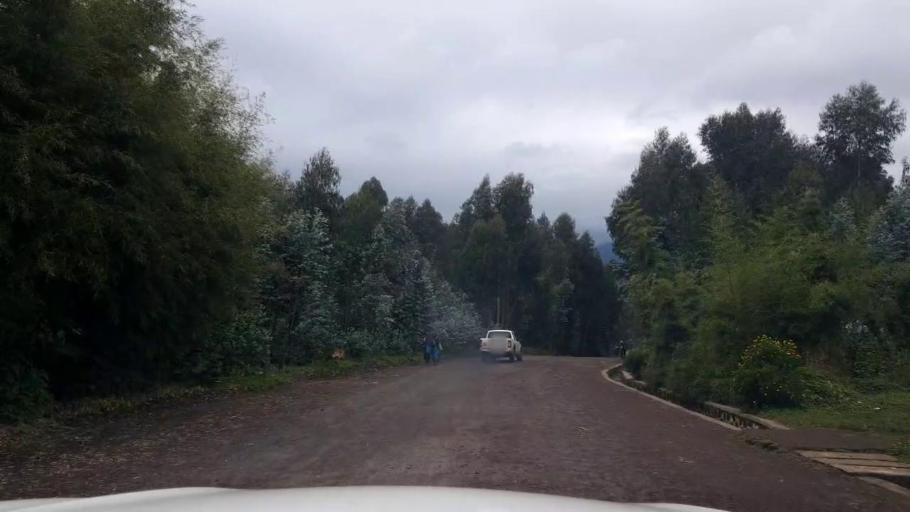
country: RW
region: Northern Province
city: Musanze
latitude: -1.4412
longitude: 29.5406
